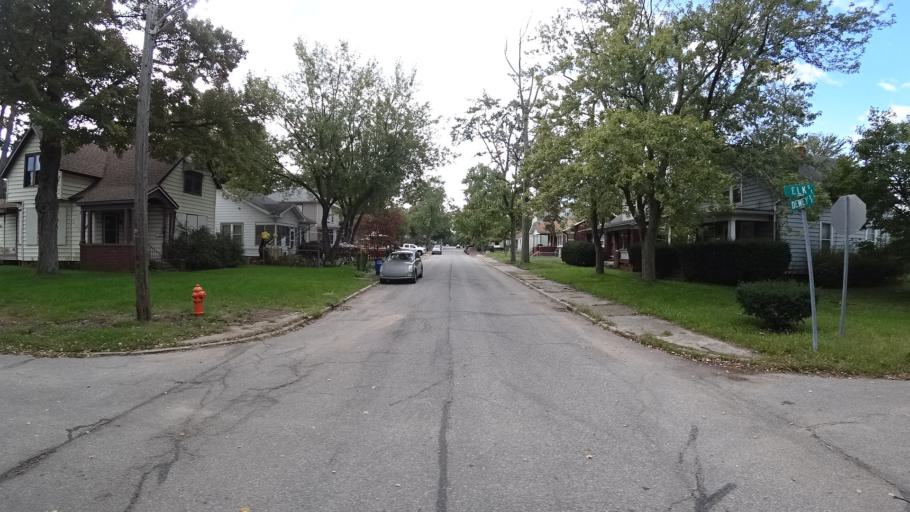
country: US
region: Indiana
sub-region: LaPorte County
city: Michigan City
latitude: 41.7092
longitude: -86.8760
